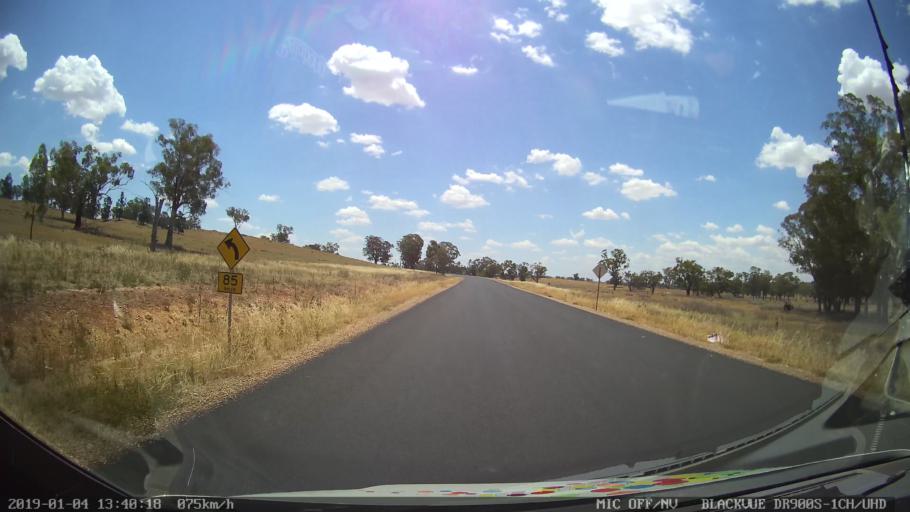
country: AU
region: New South Wales
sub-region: Dubbo Municipality
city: Dubbo
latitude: -32.5157
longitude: 148.5551
